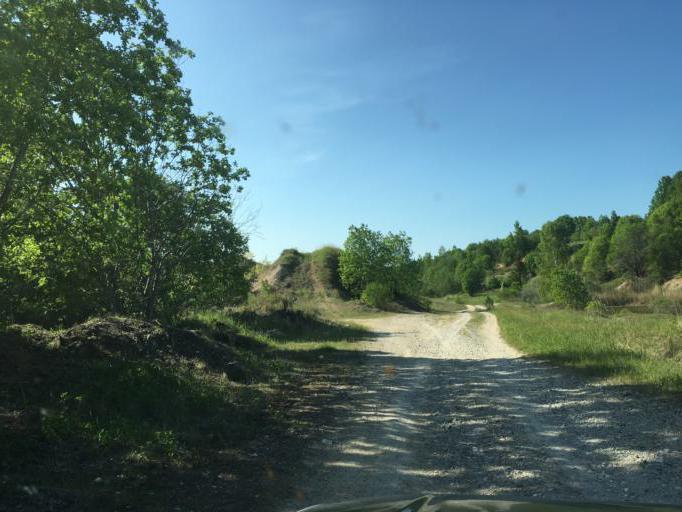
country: LV
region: Dundaga
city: Dundaga
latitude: 57.6110
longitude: 22.4410
